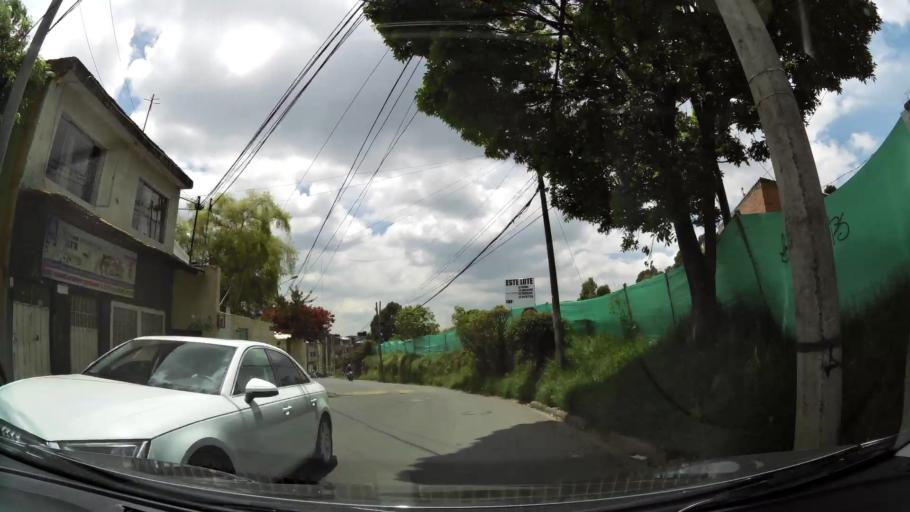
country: CO
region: Cundinamarca
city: Cota
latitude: 4.7376
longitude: -74.0789
